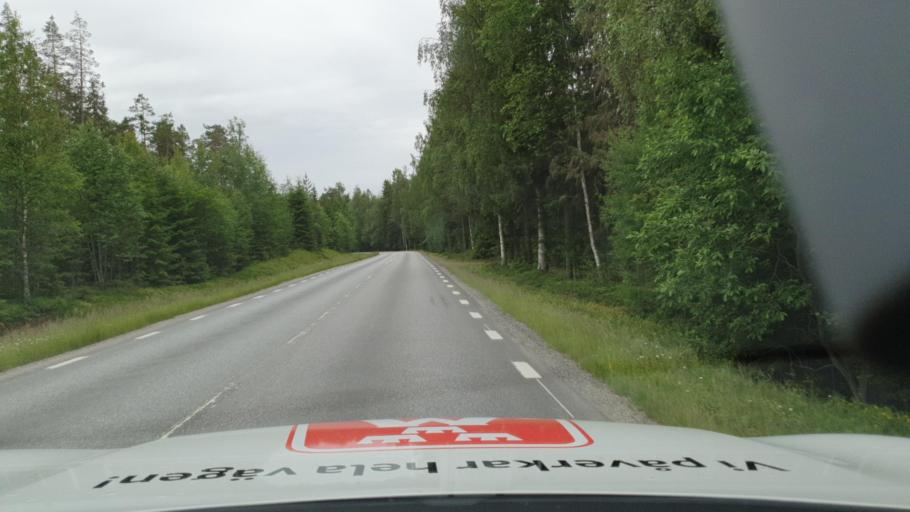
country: SE
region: Vaesterbotten
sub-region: Nordmalings Kommun
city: Nordmaling
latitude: 63.6189
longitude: 19.4202
